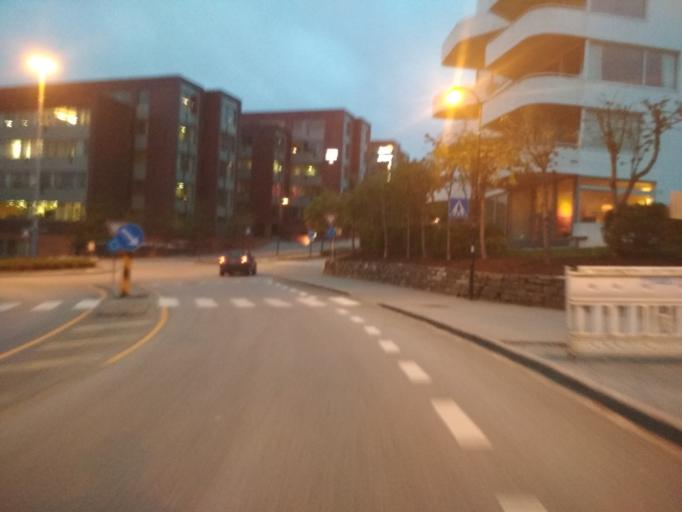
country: NO
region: Rogaland
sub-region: Stavanger
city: Stavanger
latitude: 58.9740
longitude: 5.7209
